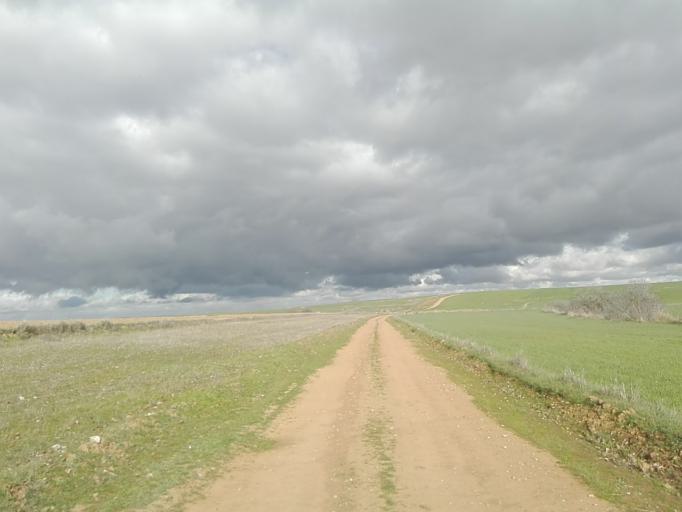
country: ES
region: Extremadura
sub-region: Provincia de Badajoz
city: Llerena
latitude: 38.2783
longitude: -6.0249
